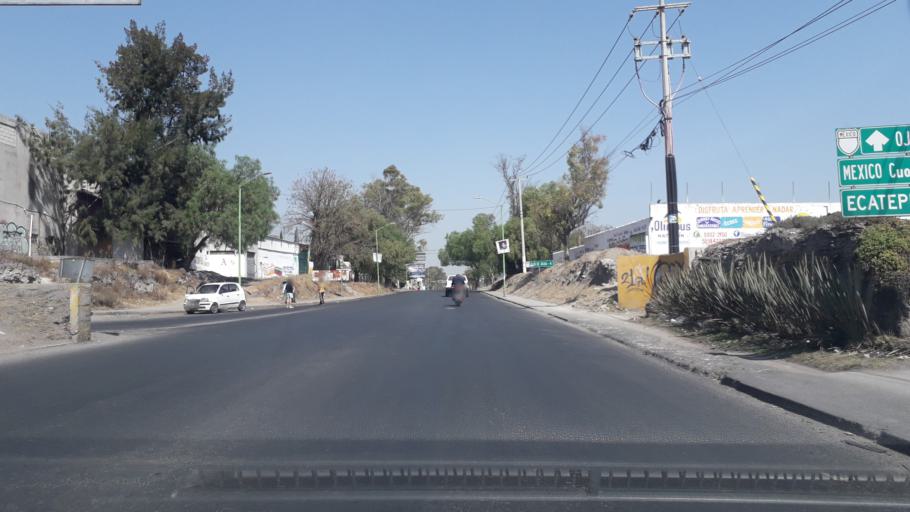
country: MX
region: Mexico
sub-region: Tecamac
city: Ojo de Agua
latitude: 19.6611
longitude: -99.0069
